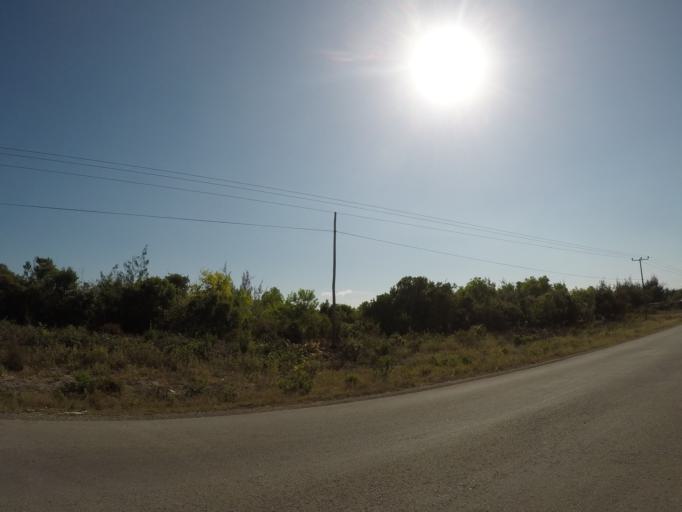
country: TZ
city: Kiwengwa
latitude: -6.1646
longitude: 39.5231
